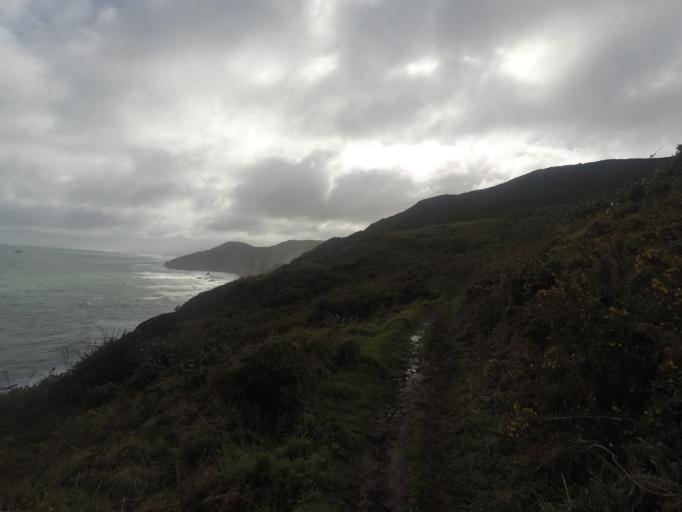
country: NZ
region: Auckland
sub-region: Auckland
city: Muriwai Beach
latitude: -36.8739
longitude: 174.4326
